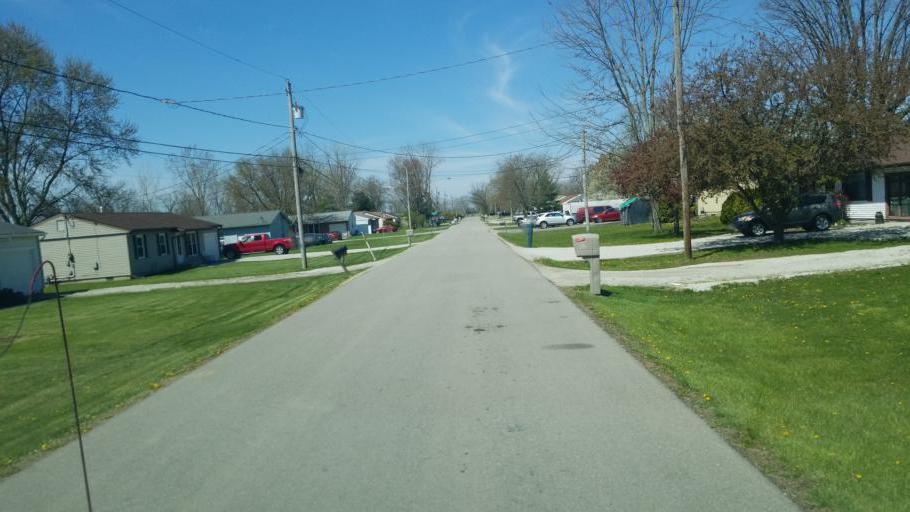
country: US
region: Ohio
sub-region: Marion County
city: Marion
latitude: 40.6426
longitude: -83.0820
